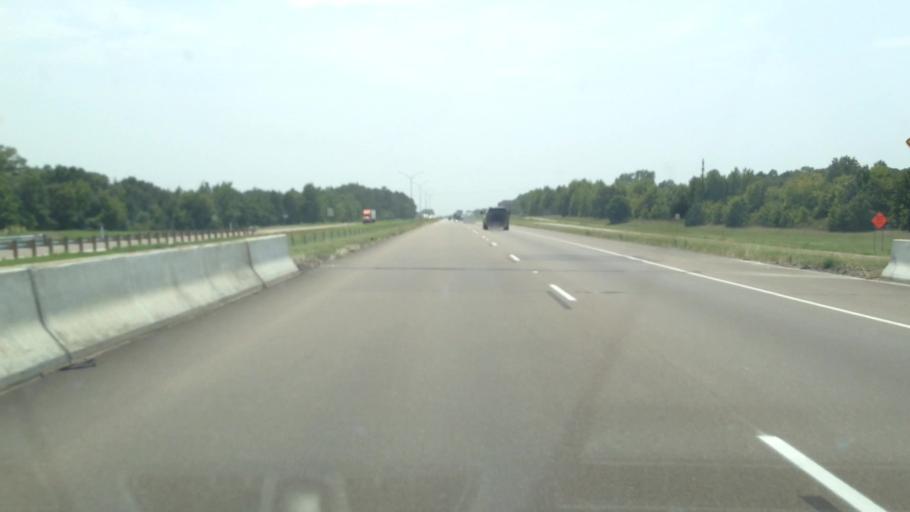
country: US
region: Texas
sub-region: Morris County
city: Omaha
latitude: 33.2439
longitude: -94.8614
